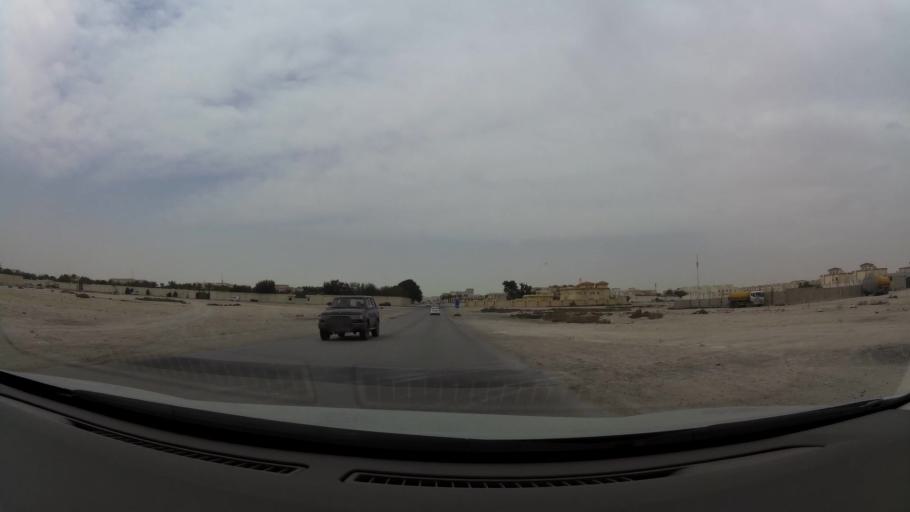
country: QA
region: Baladiyat ar Rayyan
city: Ar Rayyan
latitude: 25.2368
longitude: 51.4633
